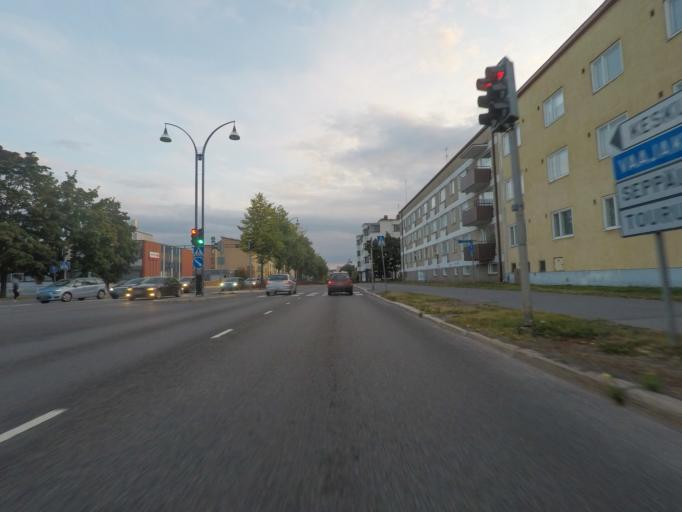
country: FI
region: Central Finland
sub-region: Jyvaeskylae
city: Jyvaeskylae
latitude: 62.2460
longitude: 25.7583
